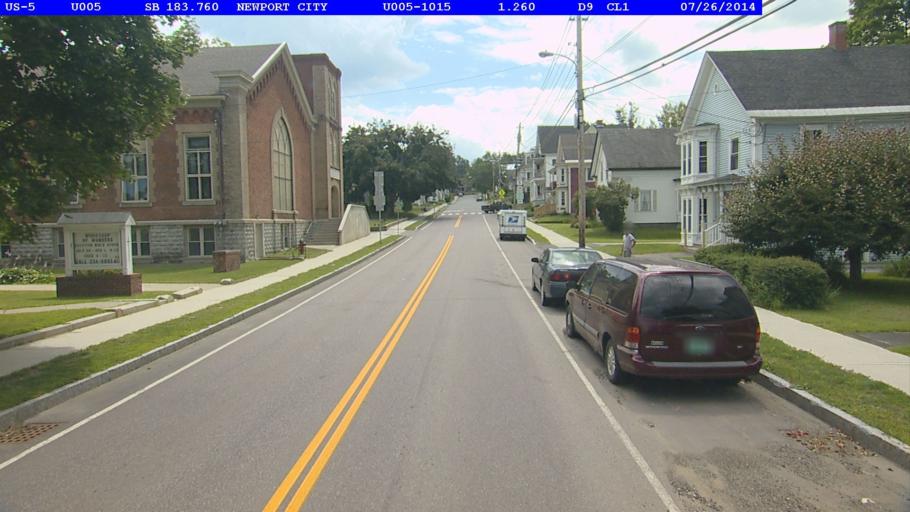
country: US
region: Vermont
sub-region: Orleans County
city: Newport
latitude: 44.9343
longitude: -72.2116
